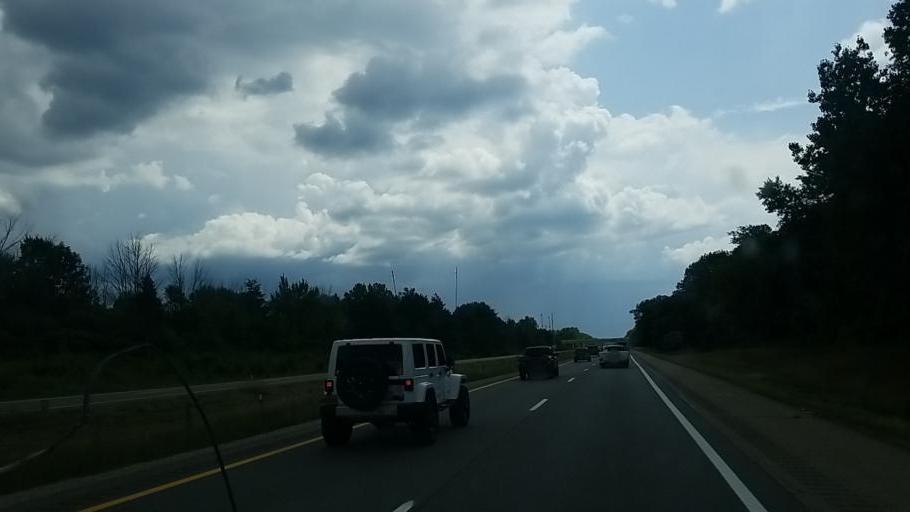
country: US
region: Michigan
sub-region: Kent County
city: Northview
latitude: 43.0040
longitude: -85.6049
